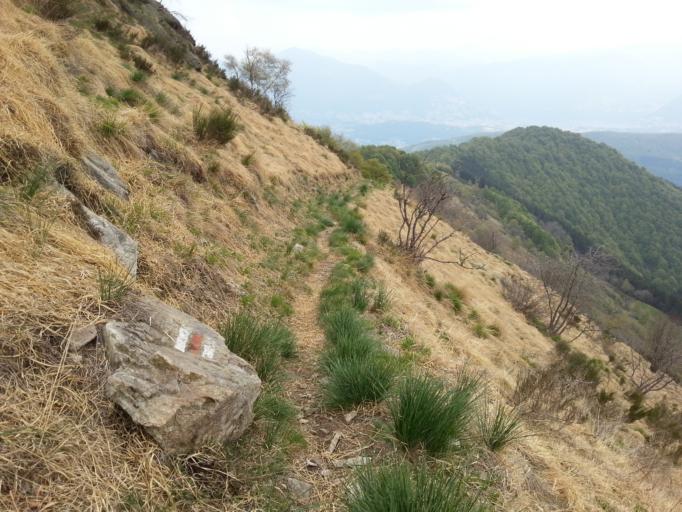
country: IT
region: Lombardy
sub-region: Provincia di Varese
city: Curiglia
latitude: 46.0537
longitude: 8.8565
